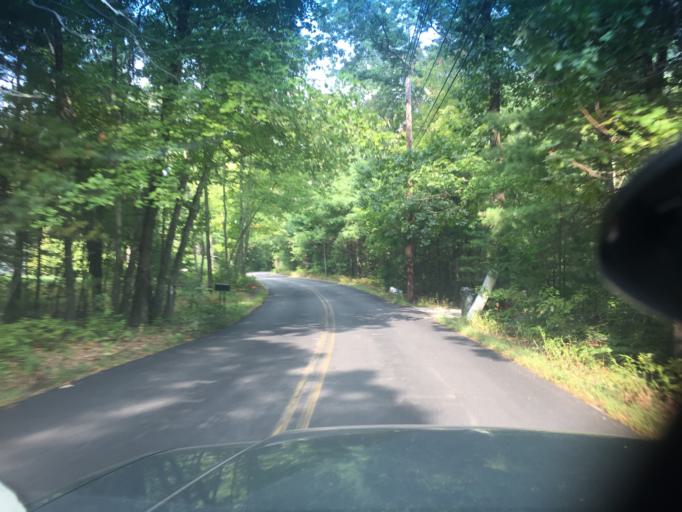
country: US
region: Massachusetts
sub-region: Norfolk County
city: Bellingham
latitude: 42.1316
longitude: -71.4613
